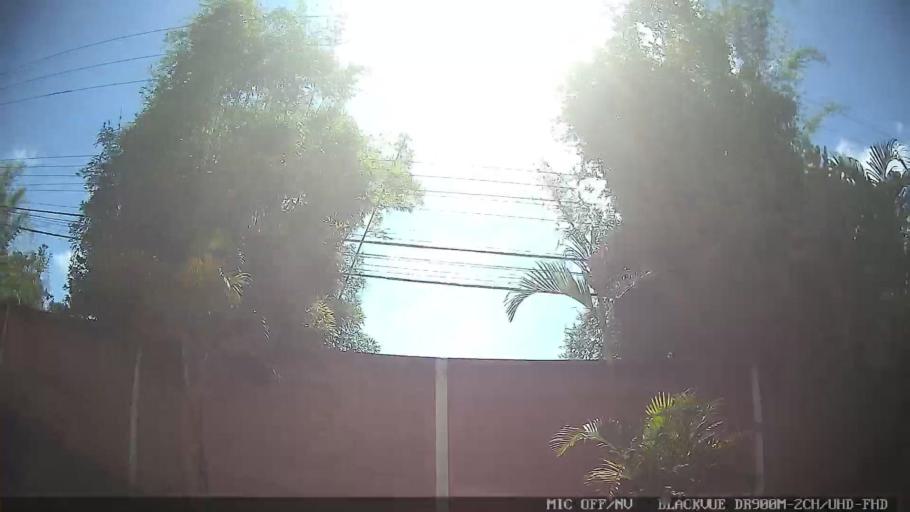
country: BR
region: Sao Paulo
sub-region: Mogi das Cruzes
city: Mogi das Cruzes
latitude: -23.6826
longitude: -46.2149
